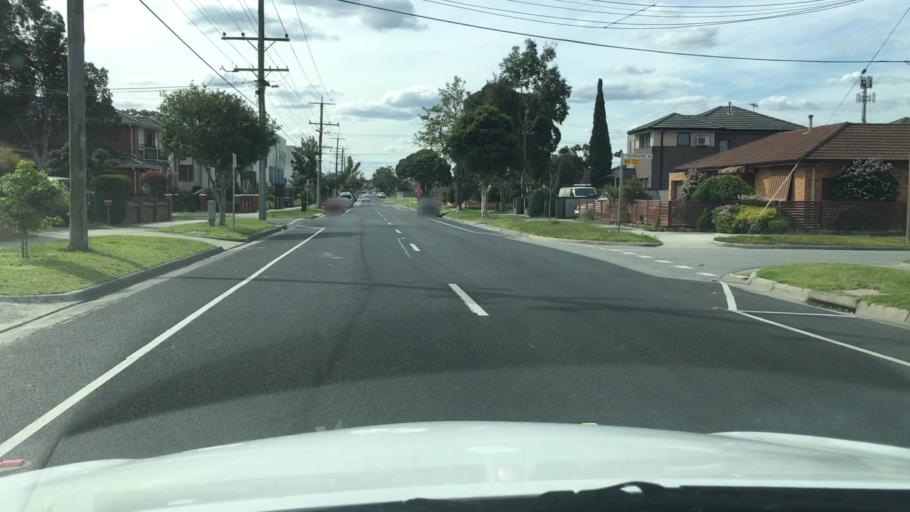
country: AU
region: Victoria
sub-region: Greater Dandenong
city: Springvale
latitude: -37.9584
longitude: 145.1573
